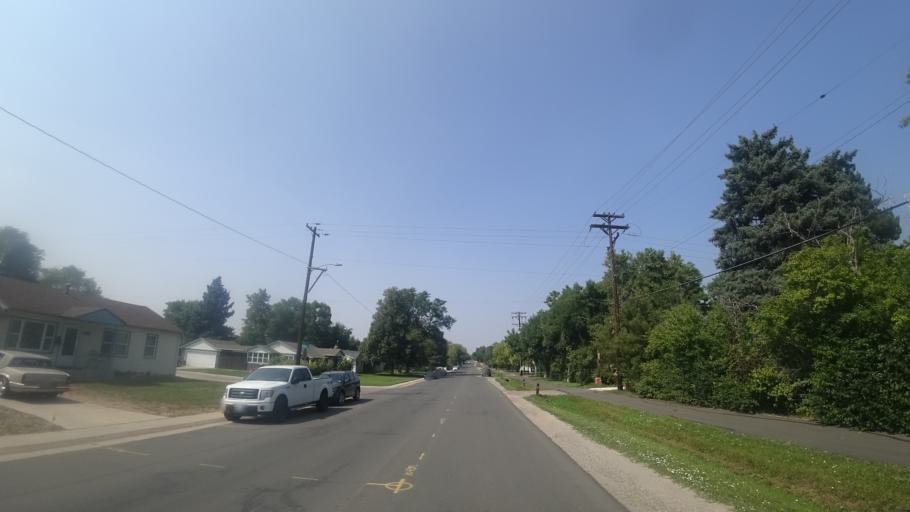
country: US
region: Colorado
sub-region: Arapahoe County
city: Englewood
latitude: 39.6274
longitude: -104.9786
